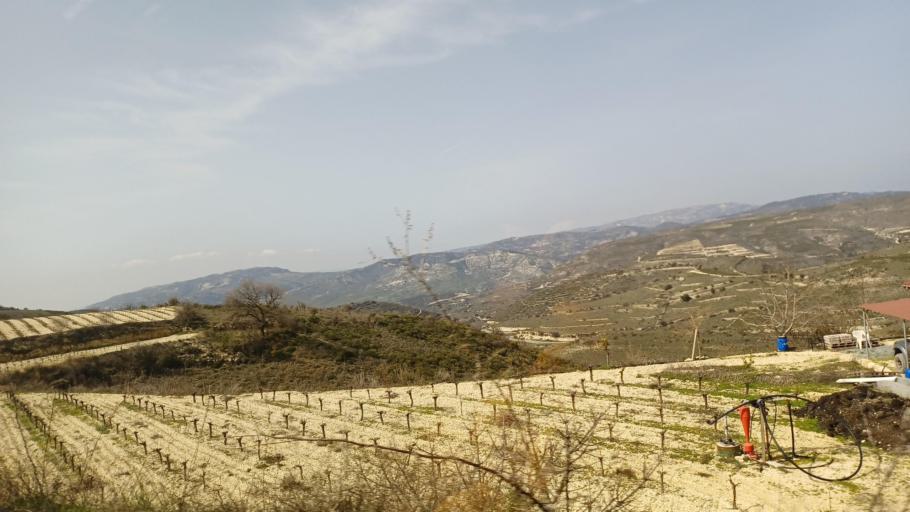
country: CY
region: Limassol
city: Pachna
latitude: 34.8069
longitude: 32.7630
